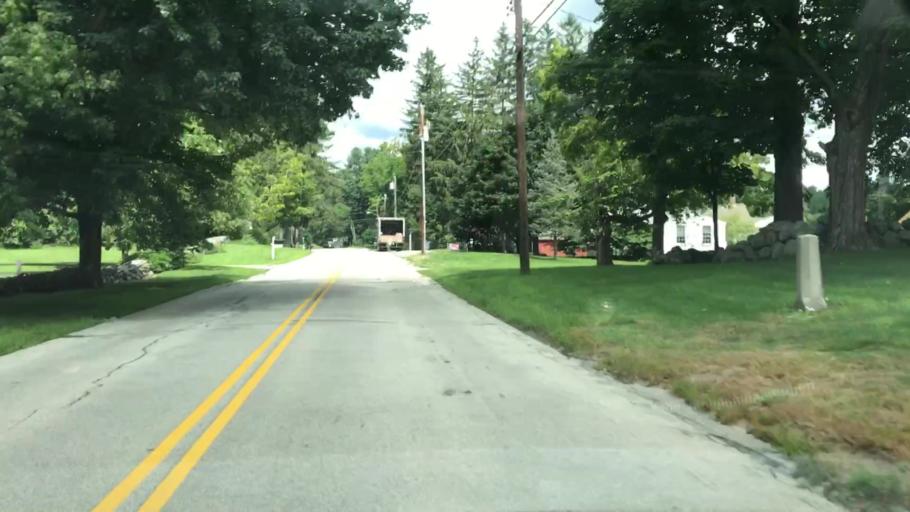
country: US
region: New Hampshire
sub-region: Hillsborough County
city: Milford
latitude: 42.8687
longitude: -71.6240
